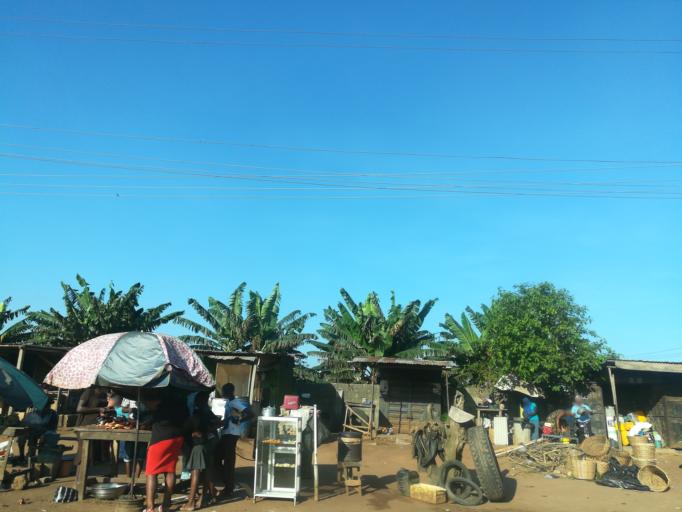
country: NG
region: Lagos
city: Ikorodu
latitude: 6.5741
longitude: 3.5286
